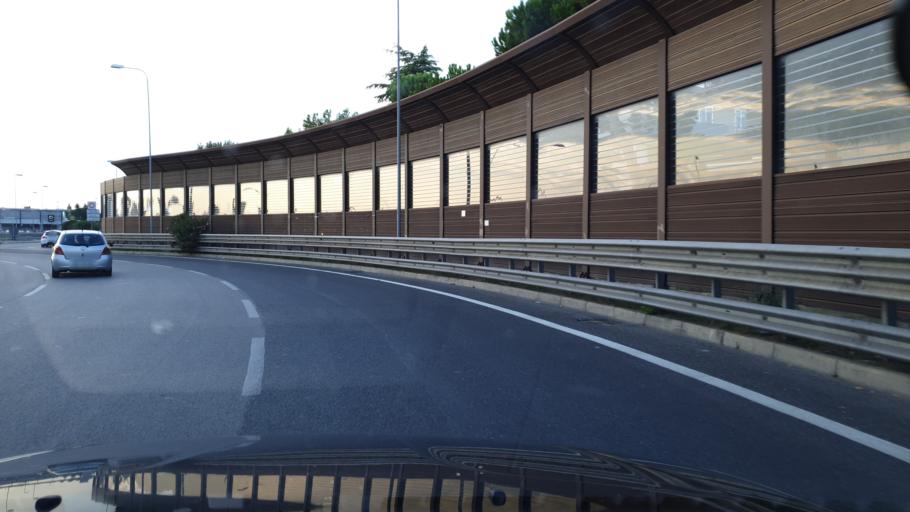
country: IT
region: Emilia-Romagna
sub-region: Provincia di Rimini
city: Rivazzurra
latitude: 44.0409
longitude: 12.5915
